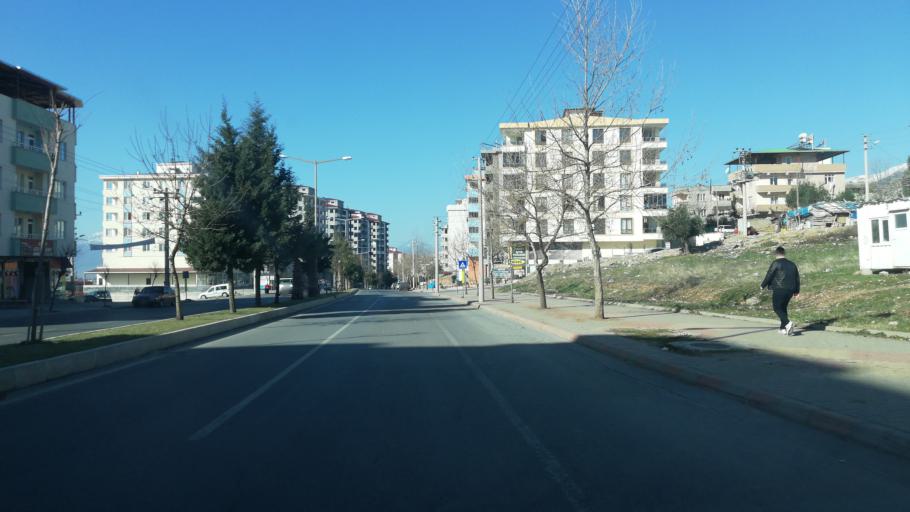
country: TR
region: Kahramanmaras
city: Kahramanmaras
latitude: 37.5820
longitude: 36.9715
